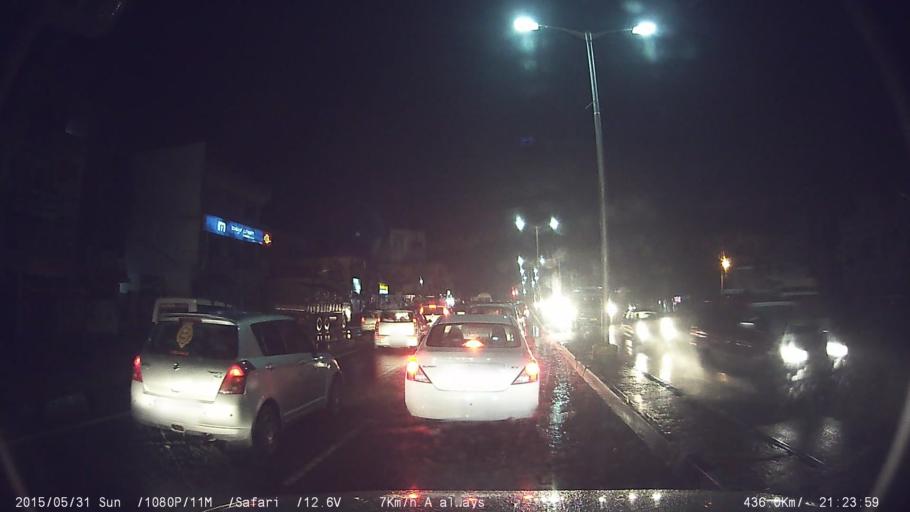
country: IN
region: Karnataka
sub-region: Ramanagara
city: Ramanagaram
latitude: 12.7205
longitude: 77.2750
